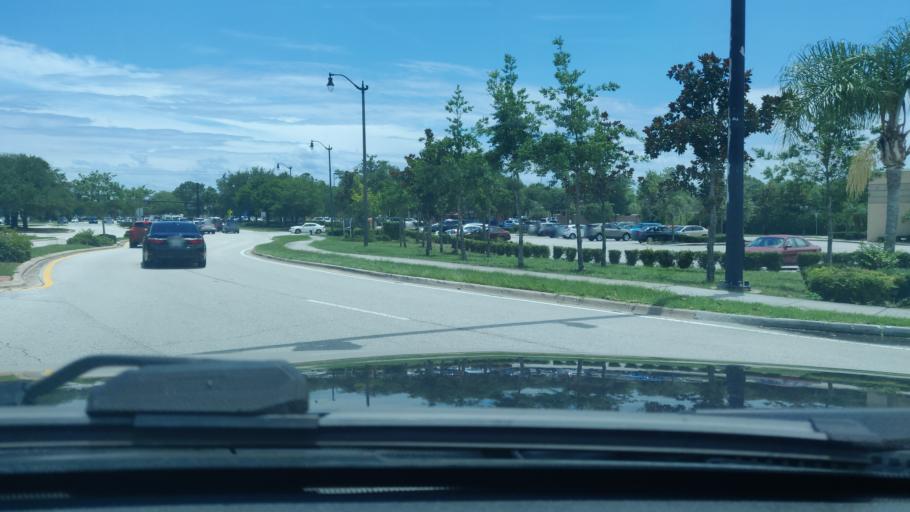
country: US
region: Florida
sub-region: Flagler County
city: Palm Coast
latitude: 29.5551
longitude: -81.2263
